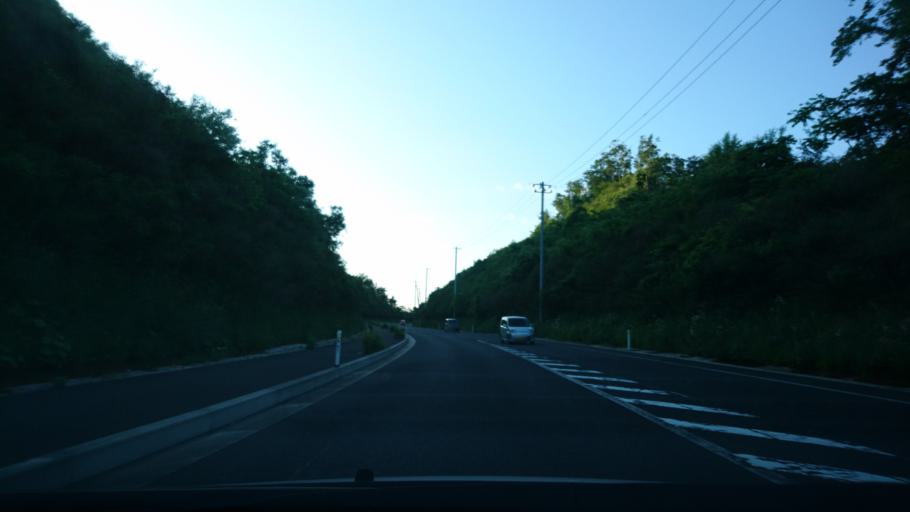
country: JP
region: Iwate
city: Ichinoseki
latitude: 38.9009
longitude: 141.1578
